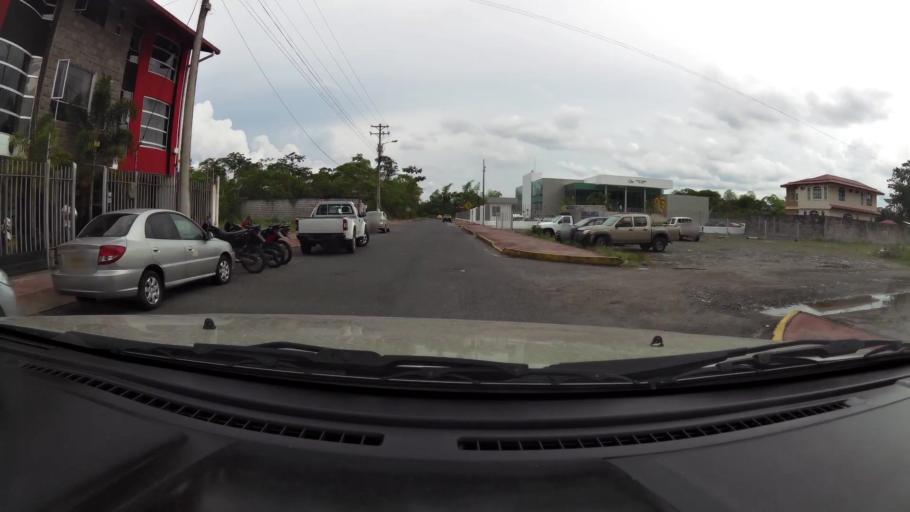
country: EC
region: Pastaza
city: Puyo
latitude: -1.5016
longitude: -78.0209
